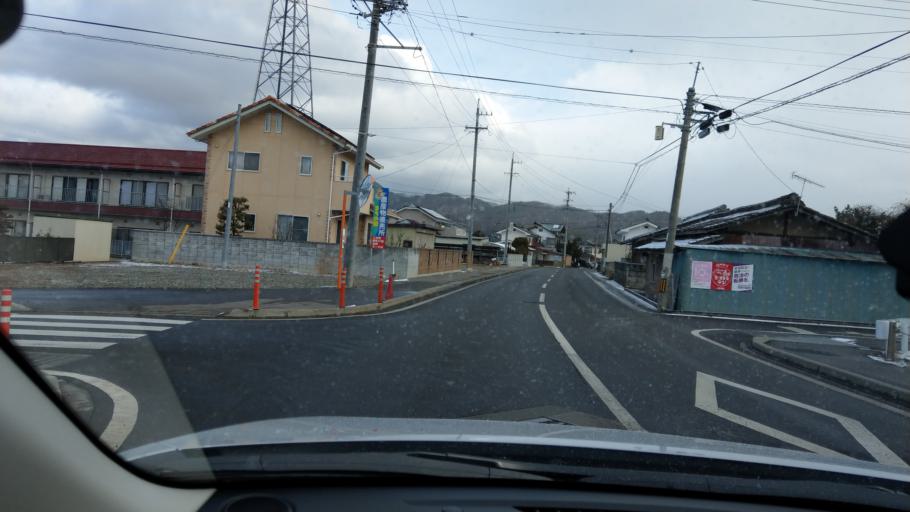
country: JP
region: Nagano
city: Saku
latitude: 36.1613
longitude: 138.4787
